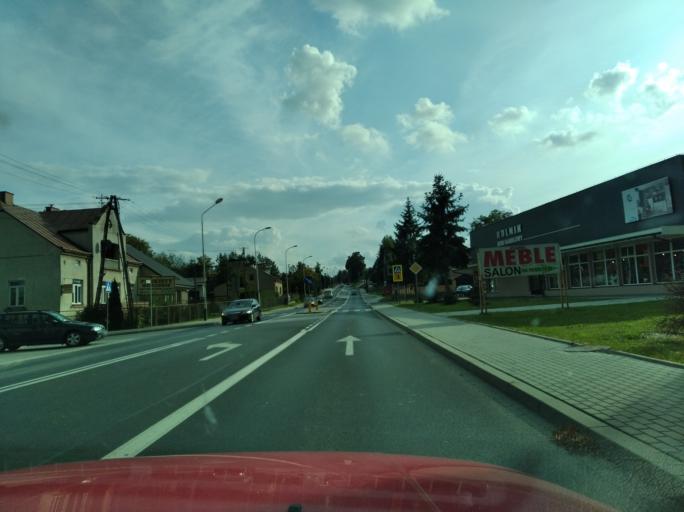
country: PL
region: Subcarpathian Voivodeship
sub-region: Powiat jaroslawski
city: Jaroslaw
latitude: 50.0066
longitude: 22.6756
